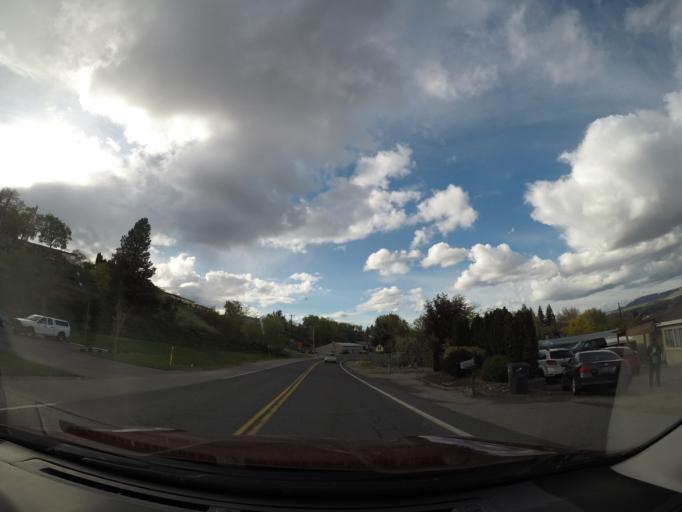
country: US
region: Washington
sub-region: Chelan County
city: South Wenatchee
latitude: 47.3961
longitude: -120.3022
